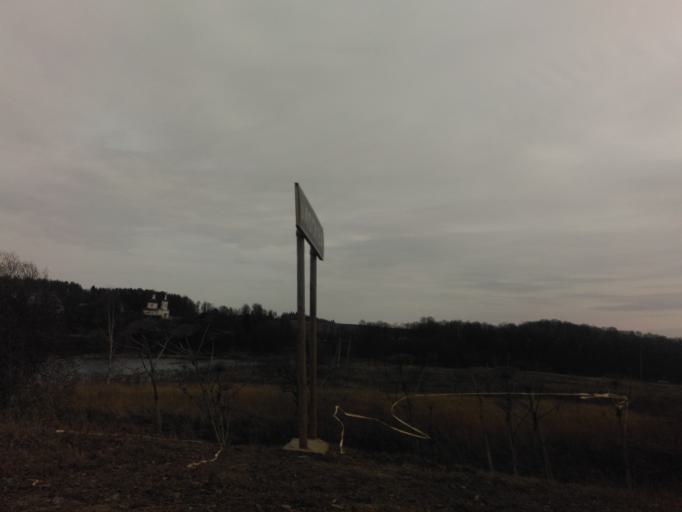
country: RU
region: Moskovskaya
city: Tuchkovo
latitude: 55.6170
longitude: 36.5061
